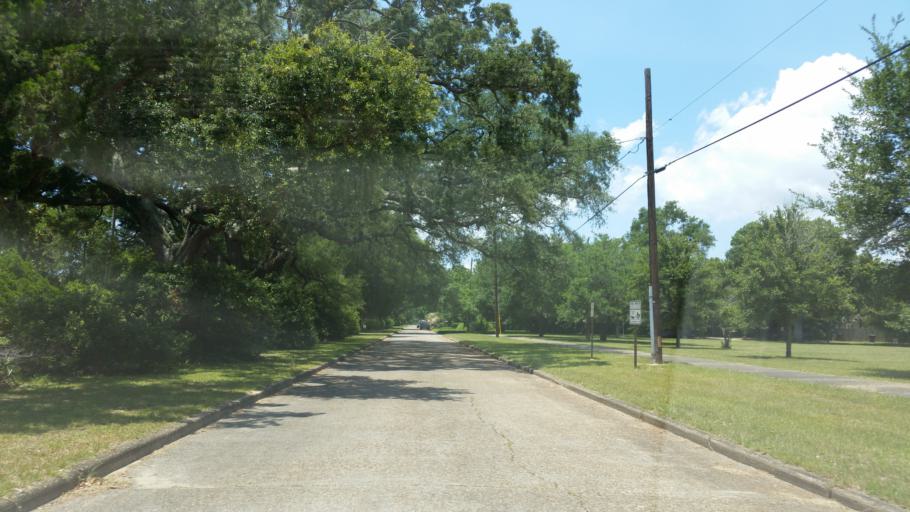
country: US
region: Florida
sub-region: Escambia County
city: East Pensacola Heights
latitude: 30.4352
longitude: -87.1996
